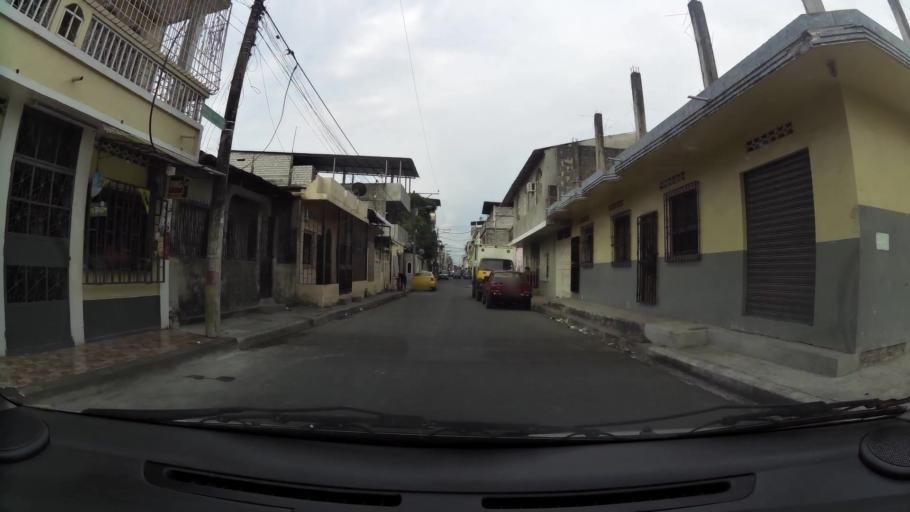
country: EC
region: Guayas
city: Guayaquil
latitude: -2.2535
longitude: -79.8976
